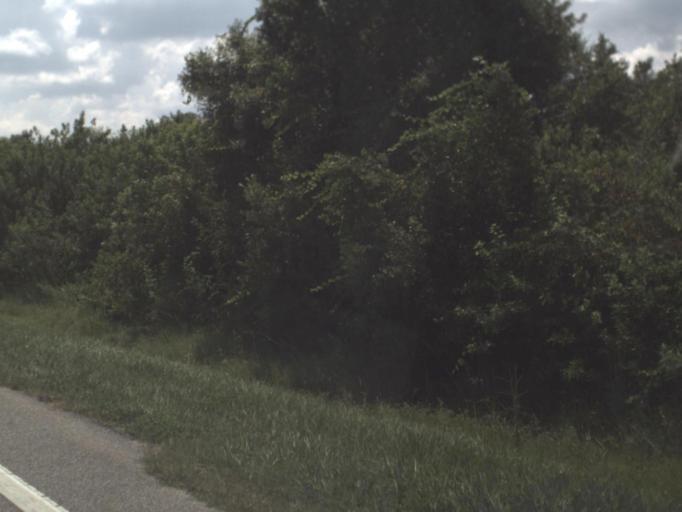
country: US
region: Florida
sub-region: Hillsborough County
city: Sun City Center
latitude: 27.7101
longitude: -82.3357
